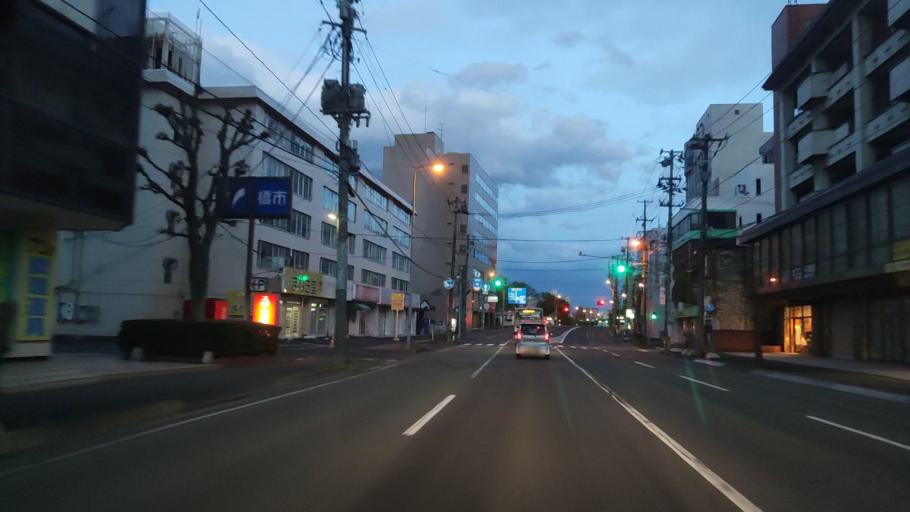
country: JP
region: Iwate
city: Morioka-shi
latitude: 39.7057
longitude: 141.1360
